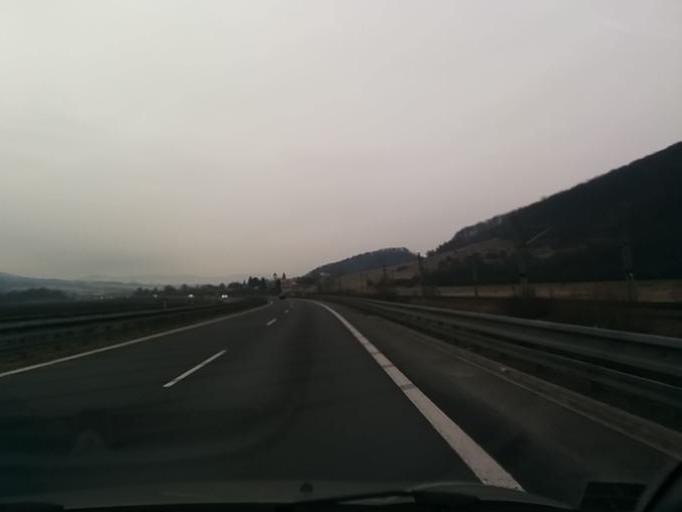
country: SK
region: Banskobystricky
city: Zarnovica
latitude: 48.5190
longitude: 18.7354
